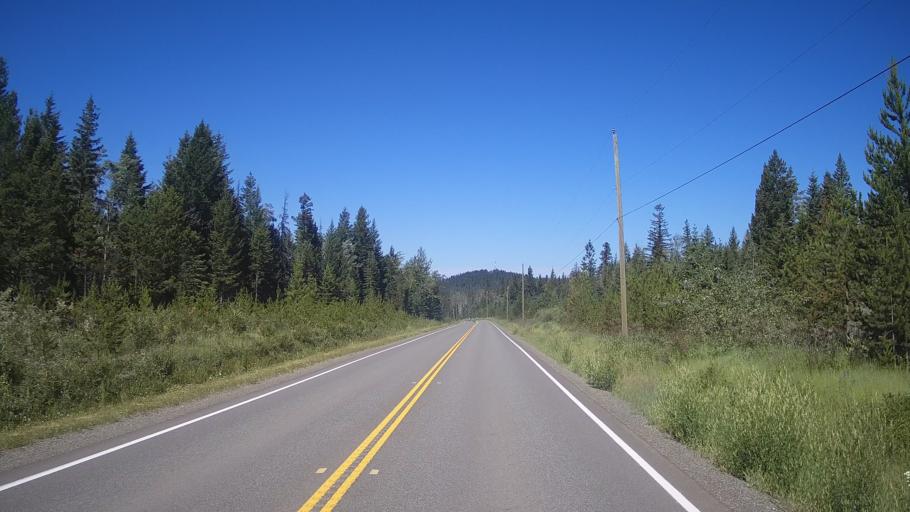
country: CA
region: British Columbia
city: Cache Creek
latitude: 51.5467
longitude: -121.0748
